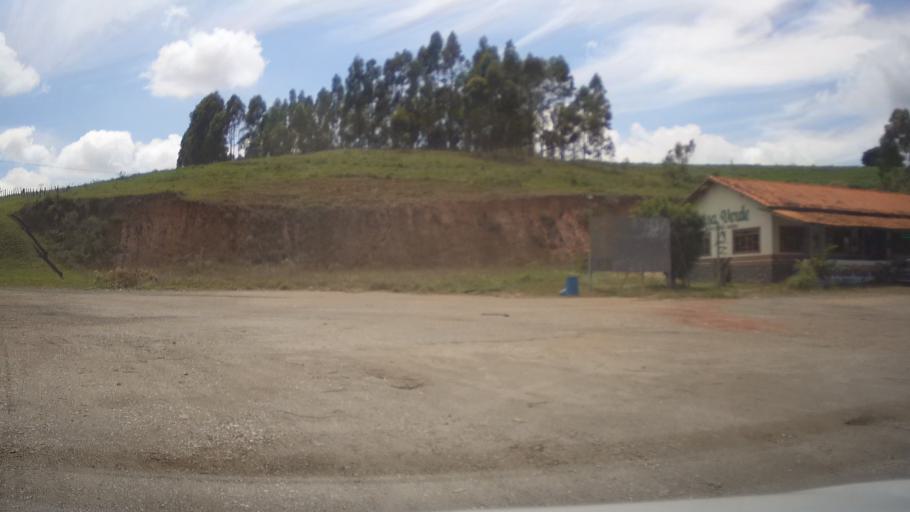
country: BR
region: Minas Gerais
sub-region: Santa Rita Do Sapucai
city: Santa Rita do Sapucai
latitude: -22.0942
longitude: -45.7112
